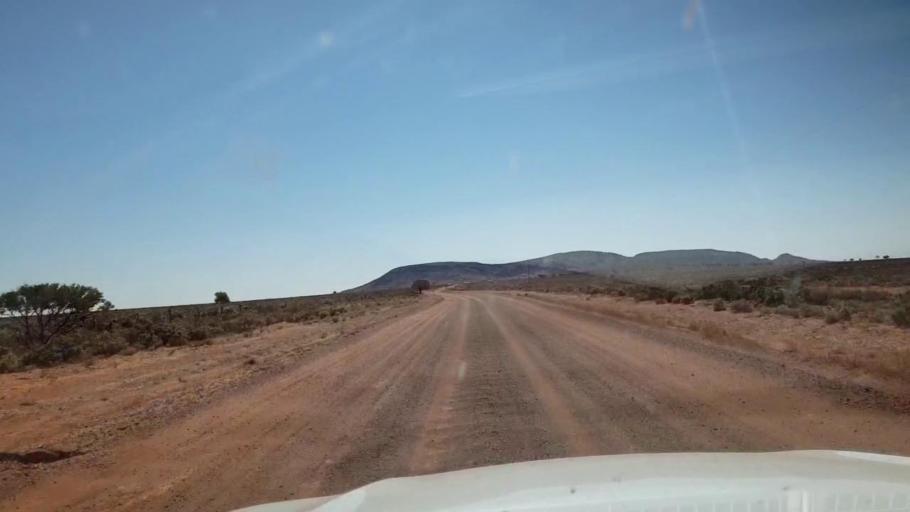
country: AU
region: South Australia
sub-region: Whyalla
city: Whyalla
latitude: -32.7116
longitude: 137.1409
